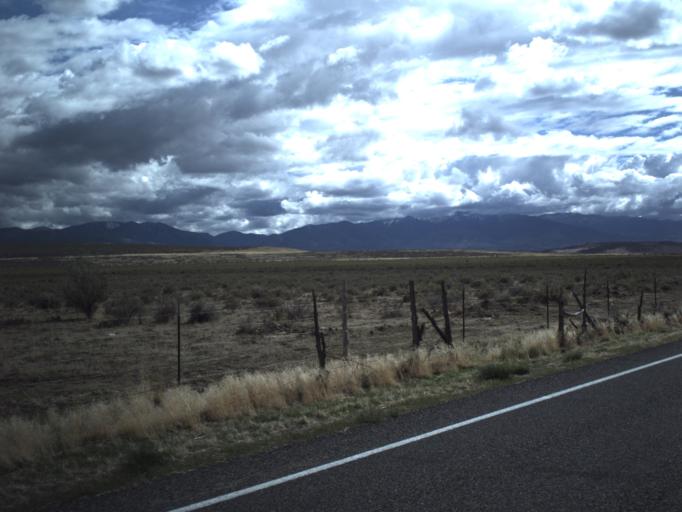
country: US
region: Utah
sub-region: Millard County
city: Fillmore
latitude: 39.0833
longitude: -112.4099
